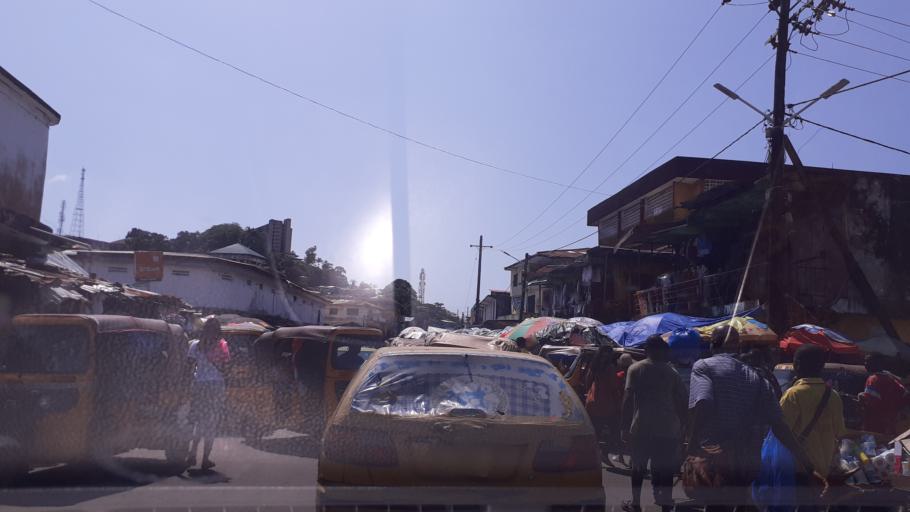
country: LR
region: Montserrado
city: Monrovia
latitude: 6.3220
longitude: -10.8074
